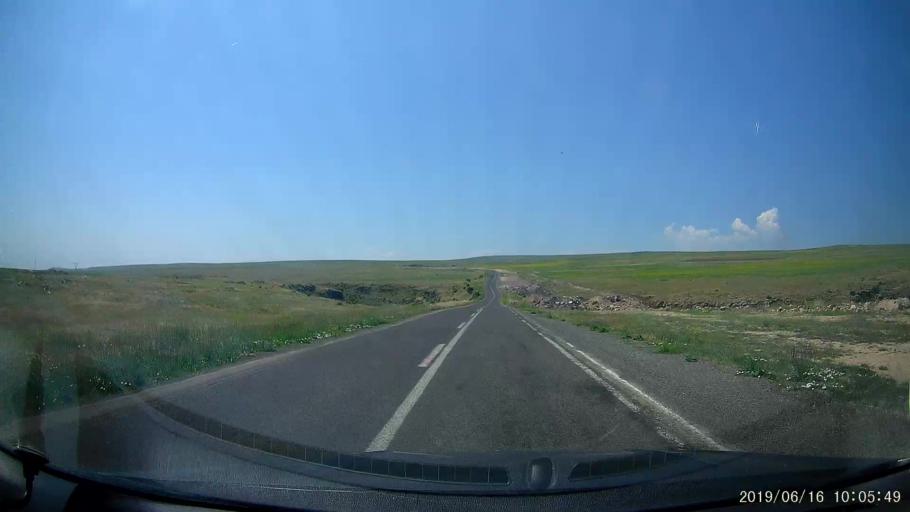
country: TR
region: Kars
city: Digor
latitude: 40.2650
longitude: 43.5399
